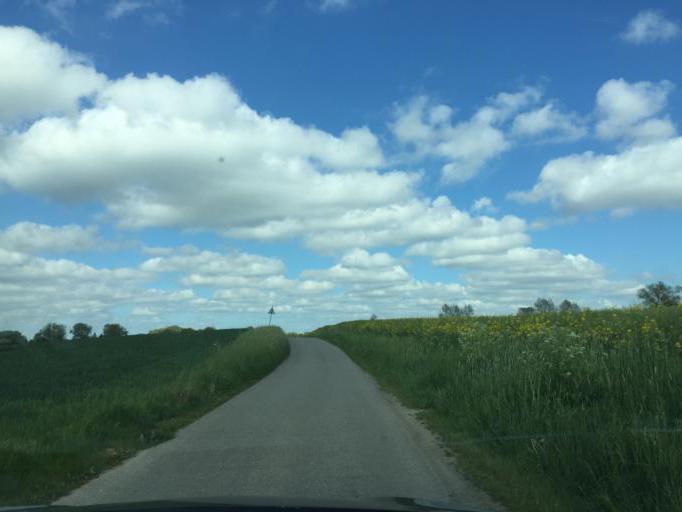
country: DK
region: South Denmark
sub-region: Assens Kommune
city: Tommerup
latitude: 55.3458
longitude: 10.2490
